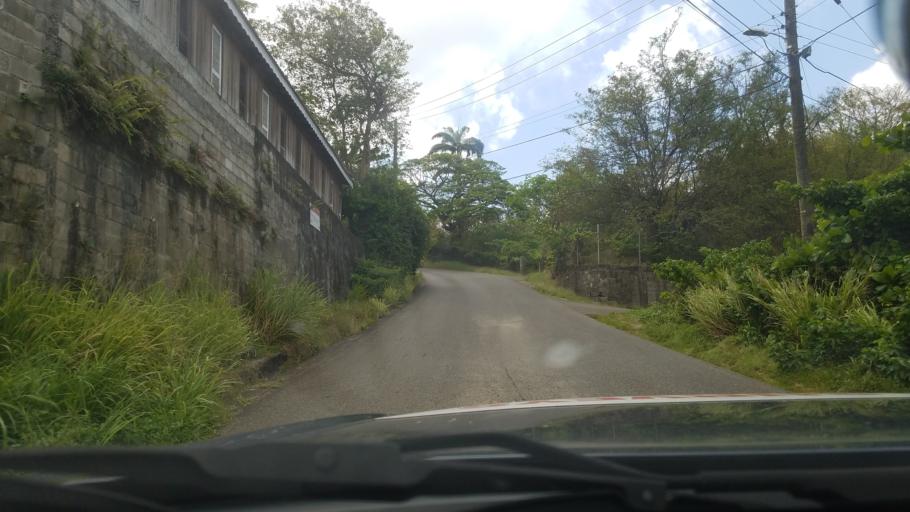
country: LC
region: Gros-Islet
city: Gros Islet
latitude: 14.0605
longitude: -60.9512
